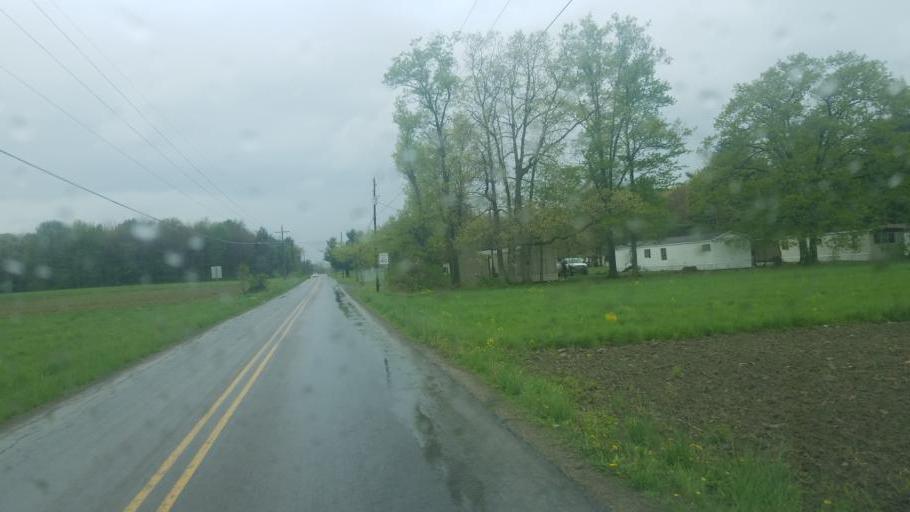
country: US
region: Pennsylvania
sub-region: Forest County
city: Tionesta
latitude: 41.3953
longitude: -79.3819
